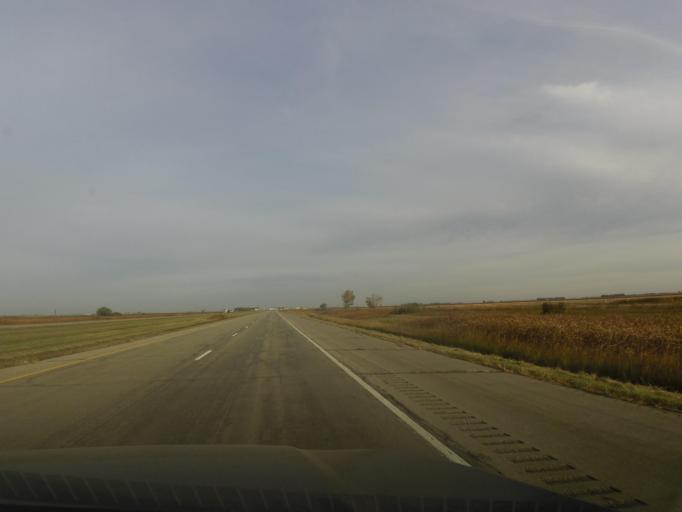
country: US
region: Minnesota
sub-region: Kittson County
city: Hallock
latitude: 48.7736
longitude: -97.2176
